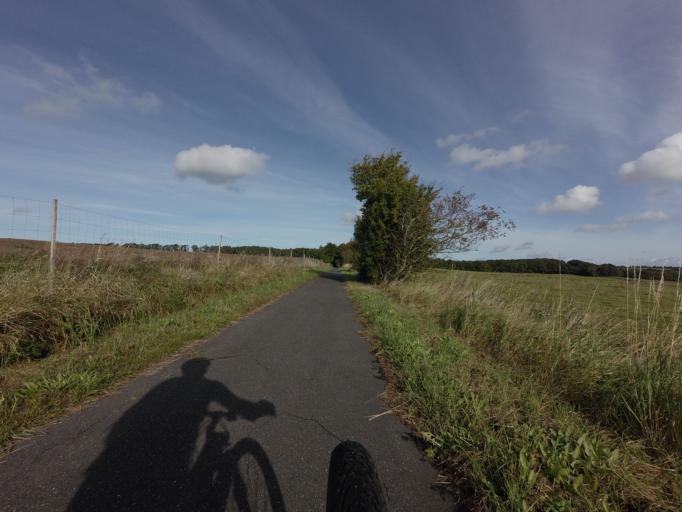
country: DK
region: Central Jutland
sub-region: Viborg Kommune
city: Bjerringbro
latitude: 56.4552
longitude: 9.5842
